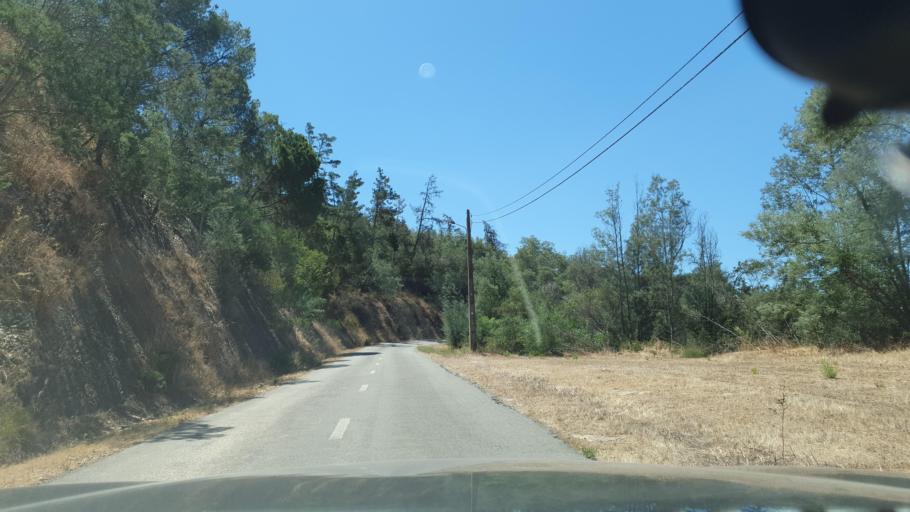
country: PT
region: Beja
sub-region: Odemira
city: Odemira
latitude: 37.5105
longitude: -8.4386
